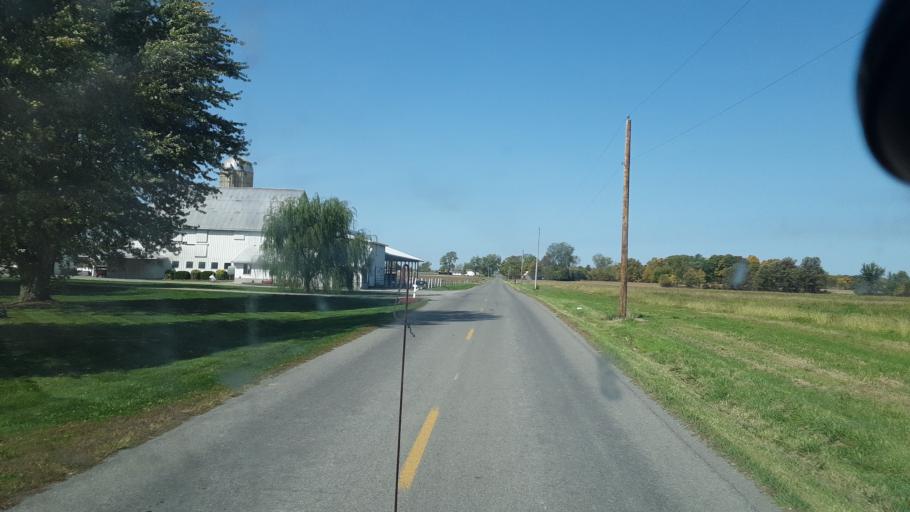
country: US
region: Ohio
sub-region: Logan County
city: Northwood
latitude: 40.4988
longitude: -83.7823
